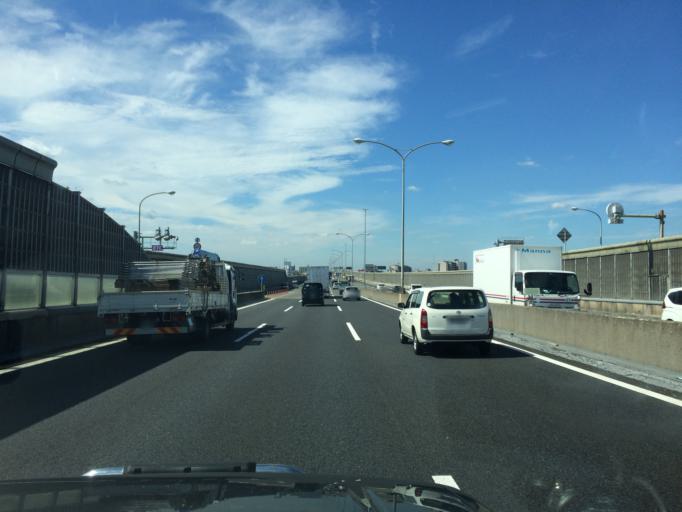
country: JP
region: Osaka
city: Matsubara
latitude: 34.5423
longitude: 135.5533
